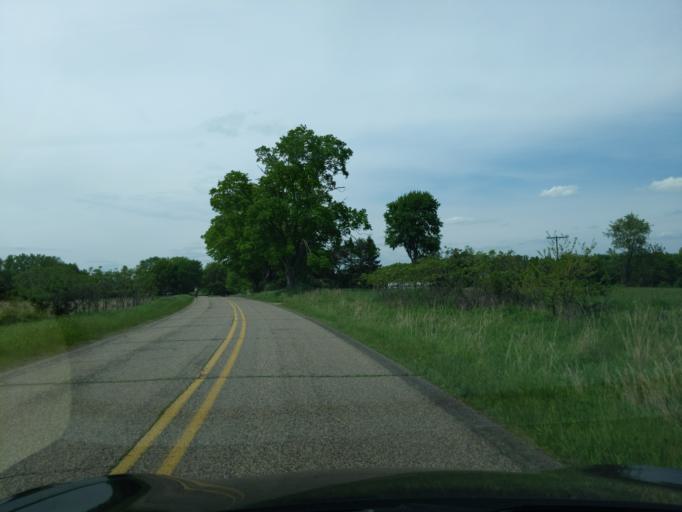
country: US
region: Michigan
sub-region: Ingham County
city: Leslie
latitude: 42.4235
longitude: -84.3336
